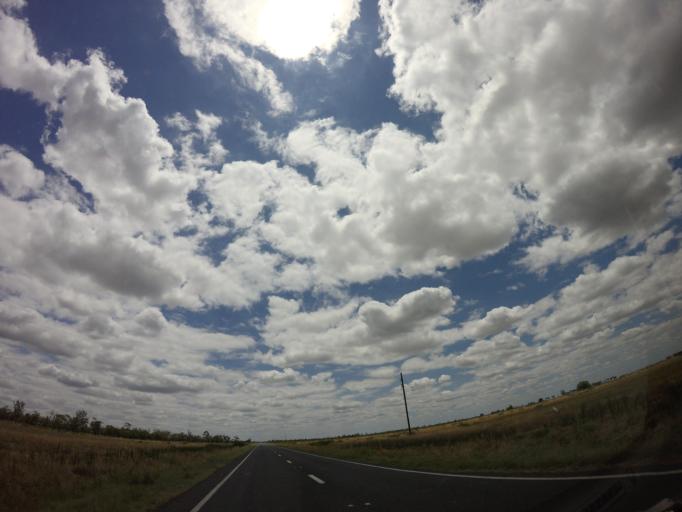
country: AU
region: New South Wales
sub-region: Moree Plains
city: Boggabilla
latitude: -28.6747
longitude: 150.3117
